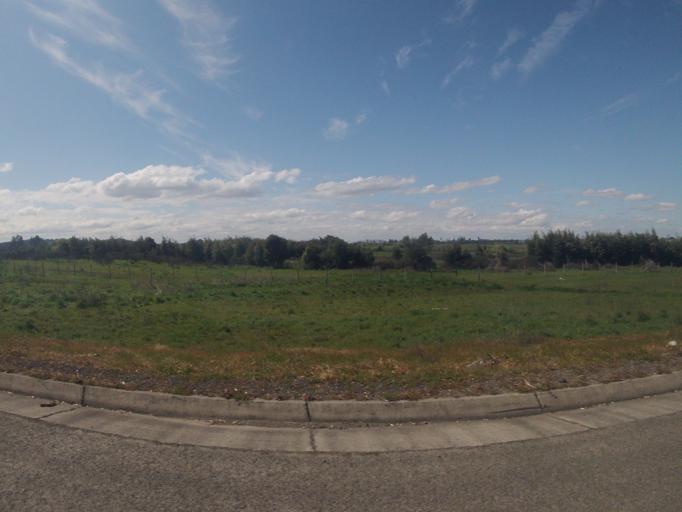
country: CL
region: Biobio
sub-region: Provincia de Biobio
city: Los Angeles
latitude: -37.4555
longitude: -72.4095
